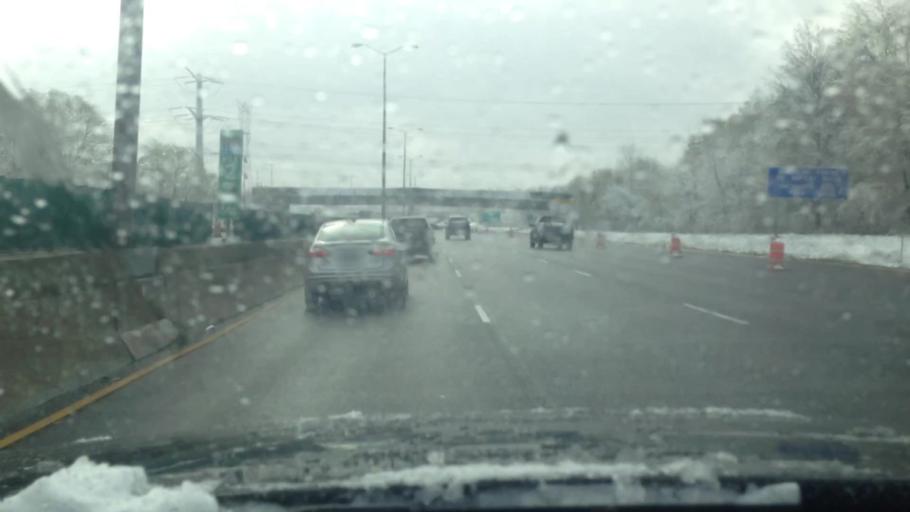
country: US
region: Illinois
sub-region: DuPage County
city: Lombard
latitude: 41.8948
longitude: -88.0380
